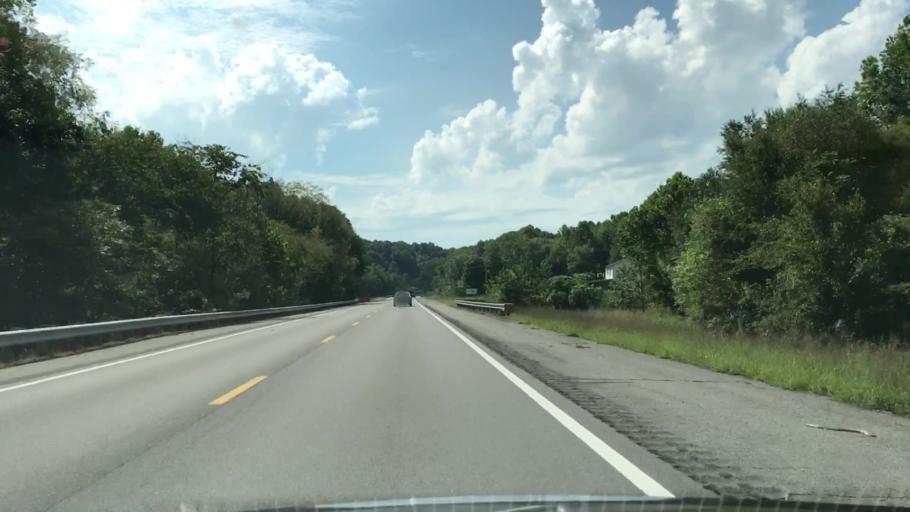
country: US
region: Tennessee
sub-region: Sumner County
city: Westmoreland
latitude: 36.6320
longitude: -86.2407
